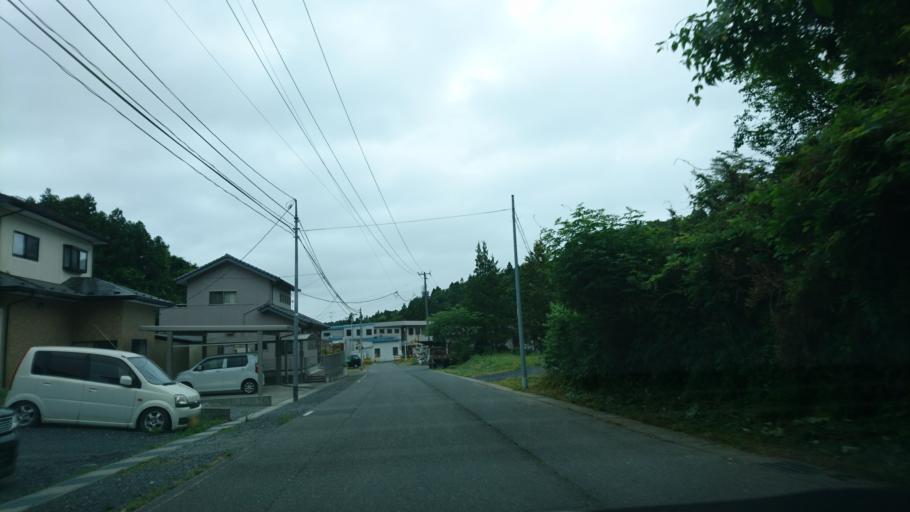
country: JP
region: Iwate
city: Ichinoseki
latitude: 38.9031
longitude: 141.1882
